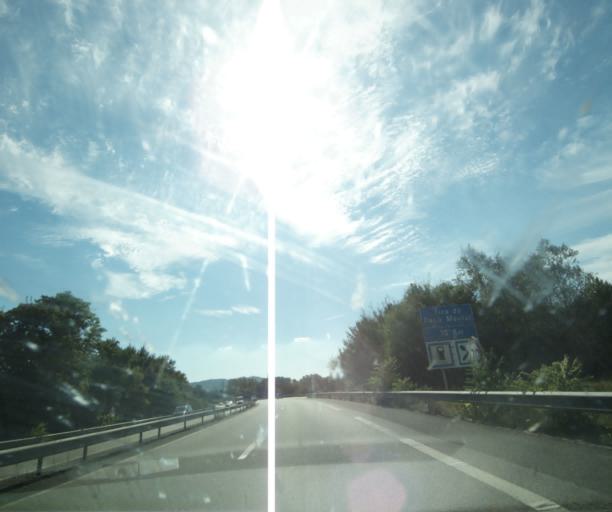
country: FR
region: Limousin
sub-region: Departement de la Correze
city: Varetz
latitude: 45.1658
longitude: 1.4802
